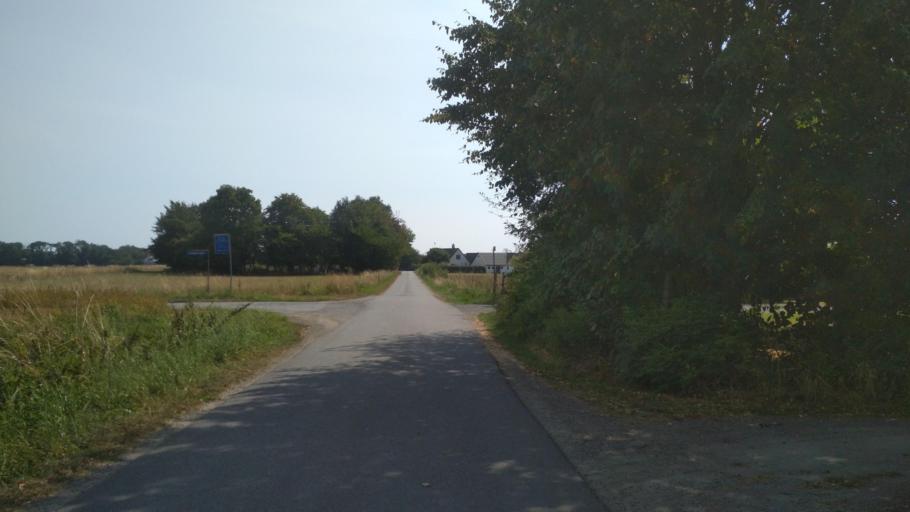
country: DK
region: Capital Region
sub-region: Bornholm Kommune
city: Akirkeby
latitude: 55.0537
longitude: 14.9405
